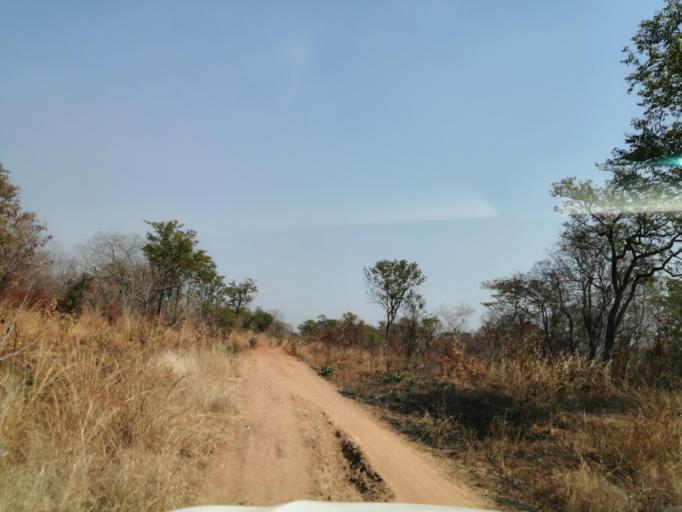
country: ZM
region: Eastern
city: Nyimba
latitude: -14.4050
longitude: 29.9875
